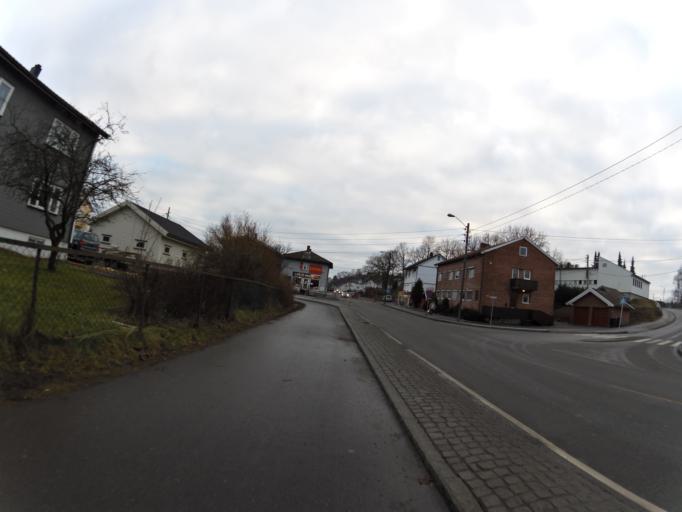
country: NO
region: Ostfold
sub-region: Fredrikstad
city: Fredrikstad
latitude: 59.2181
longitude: 10.9062
